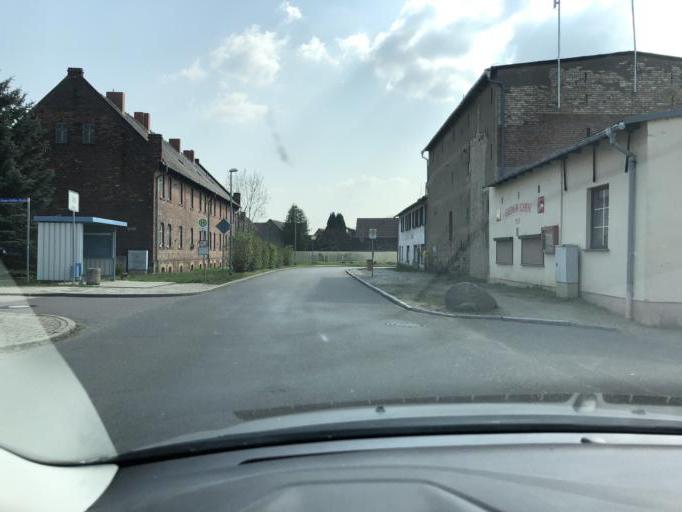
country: DE
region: Saxony-Anhalt
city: Niemberg
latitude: 51.5927
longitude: 12.0715
